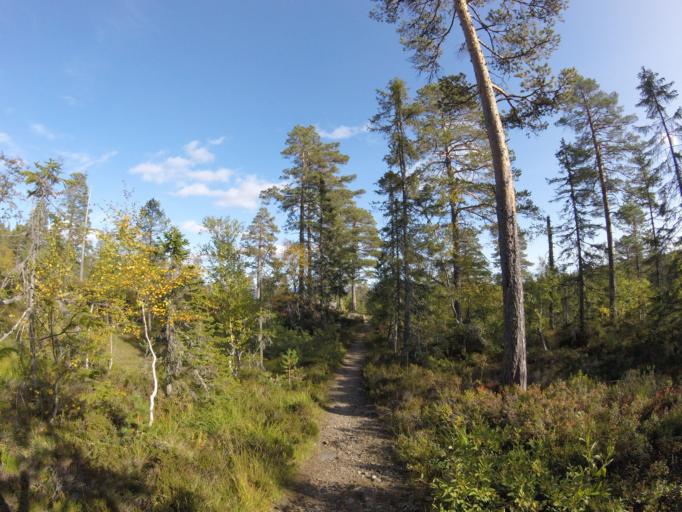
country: NO
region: Buskerud
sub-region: Kongsberg
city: Kongsberg
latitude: 59.6650
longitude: 9.5909
